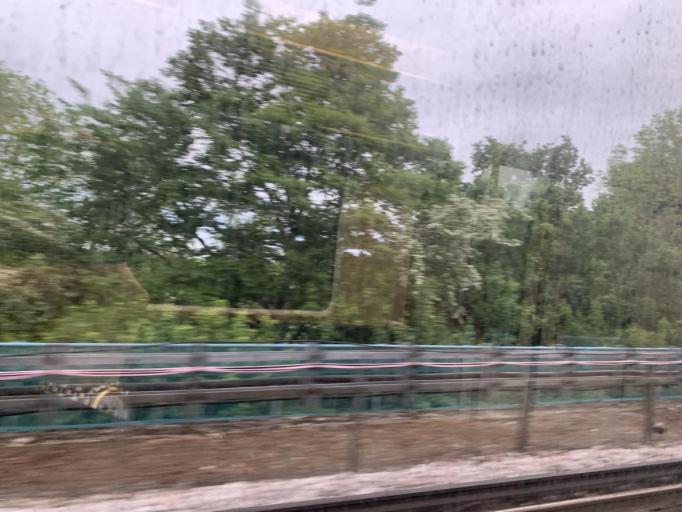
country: GB
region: England
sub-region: Essex
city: Buckhurst Hill
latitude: 51.6184
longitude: 0.0518
